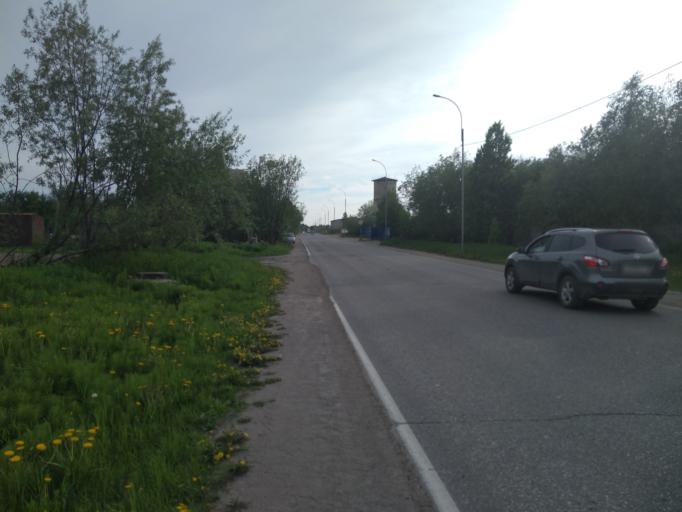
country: RU
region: Komi Republic
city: Pechora
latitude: 65.1491
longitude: 57.2157
